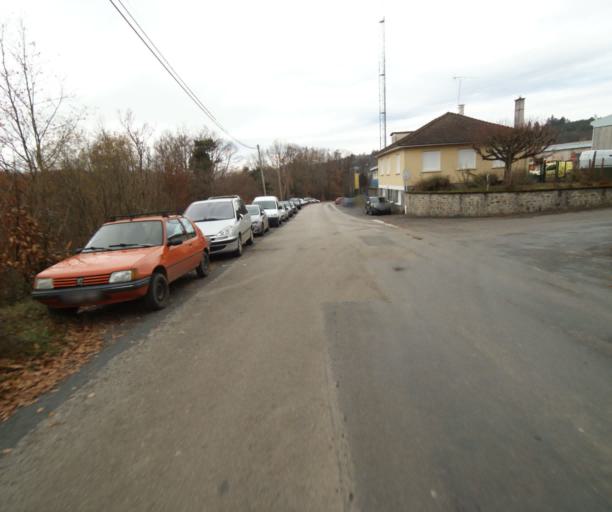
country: FR
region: Limousin
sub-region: Departement de la Correze
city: Tulle
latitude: 45.2699
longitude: 1.7357
